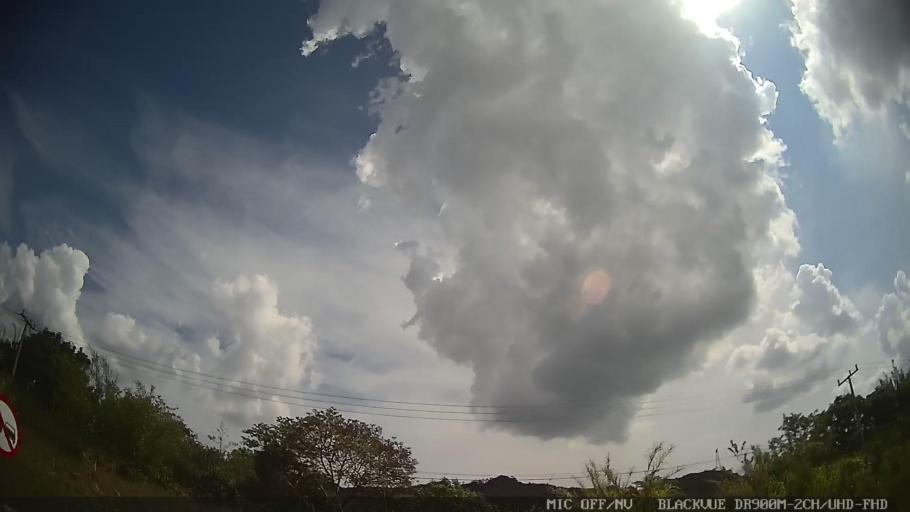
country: BR
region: Sao Paulo
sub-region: Braganca Paulista
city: Braganca Paulista
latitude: -22.9684
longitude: -46.5770
